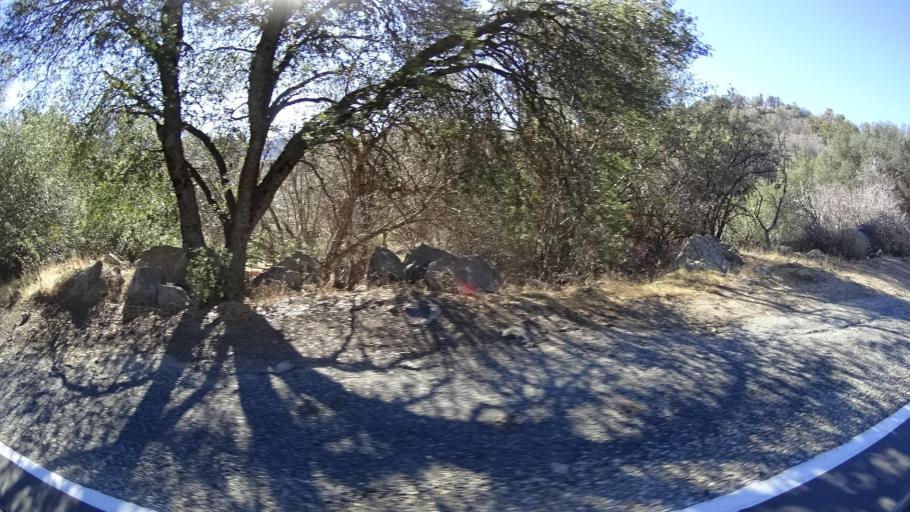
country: US
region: California
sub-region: Kern County
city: Alta Sierra
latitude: 35.7068
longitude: -118.7461
